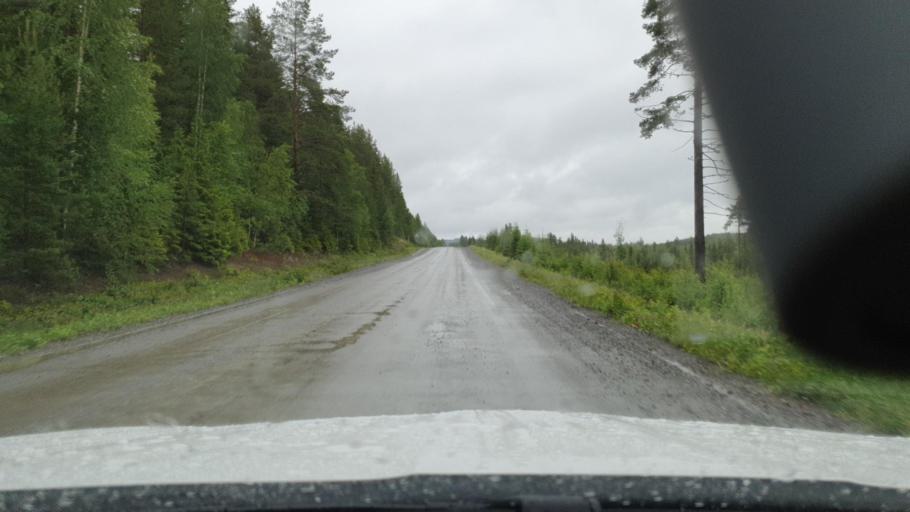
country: SE
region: Vaesterbotten
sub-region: Skelleftea Kommun
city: Burtraesk
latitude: 64.3748
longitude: 20.3626
